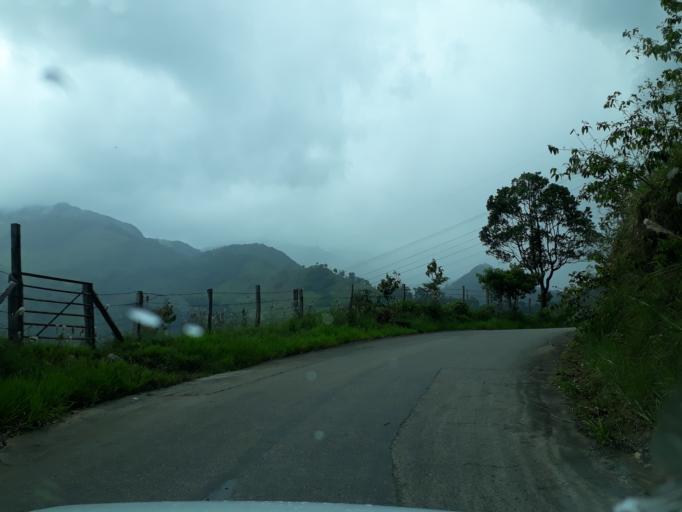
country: CO
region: Cundinamarca
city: Medina
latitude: 4.5863
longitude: -73.3700
